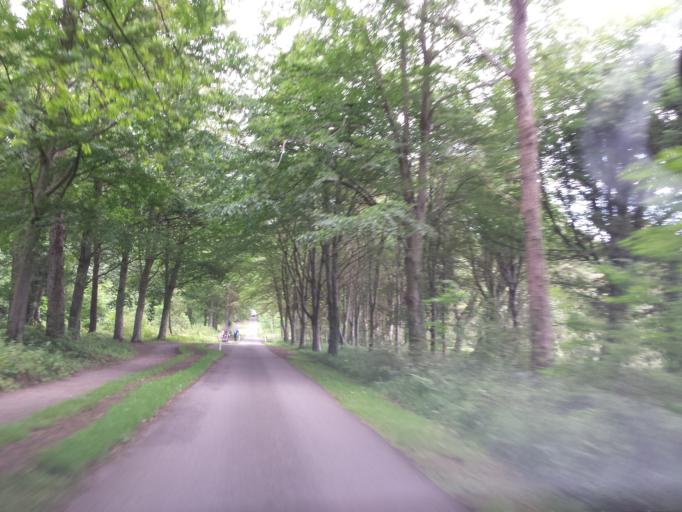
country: GB
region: Scotland
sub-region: South Ayrshire
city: Girvan
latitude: 55.3474
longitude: -4.7999
